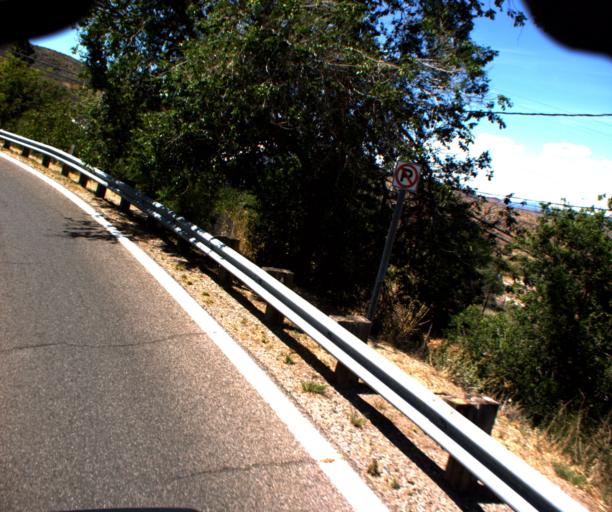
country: US
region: Arizona
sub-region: Yavapai County
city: Clarkdale
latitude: 34.7518
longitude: -112.1046
